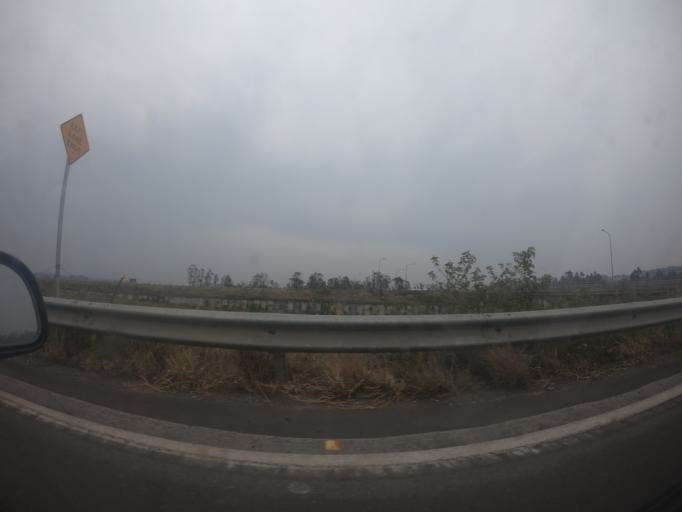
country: AU
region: New South Wales
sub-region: Shellharbour
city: Albion Park Rail
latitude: -34.5746
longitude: 150.8209
